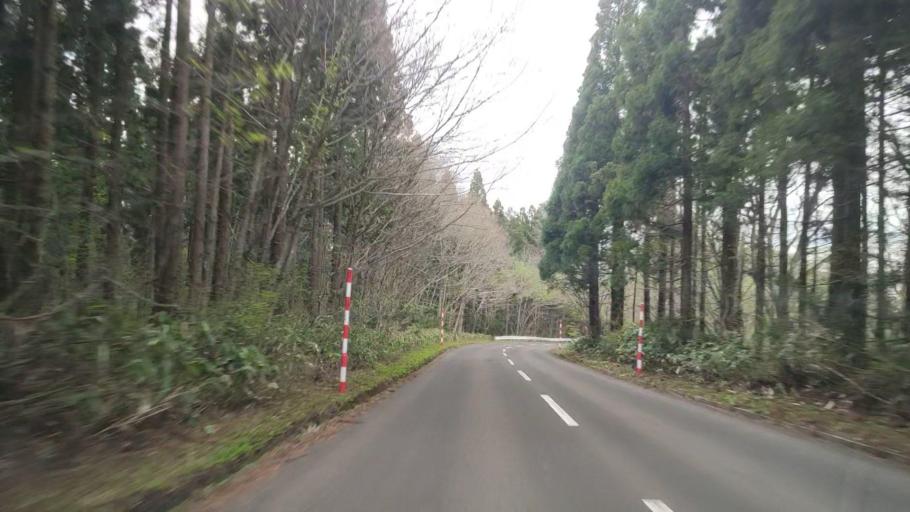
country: JP
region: Akita
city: Hanawa
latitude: 40.3911
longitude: 140.7950
